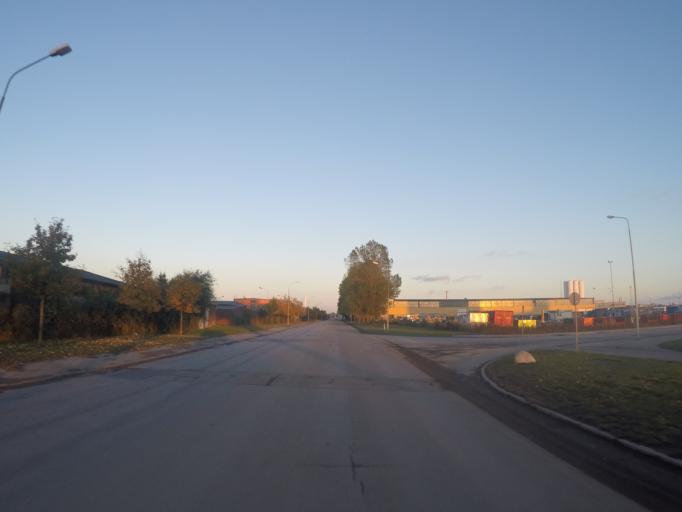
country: SE
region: Skane
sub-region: Malmo
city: Malmoe
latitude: 55.6281
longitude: 13.0174
